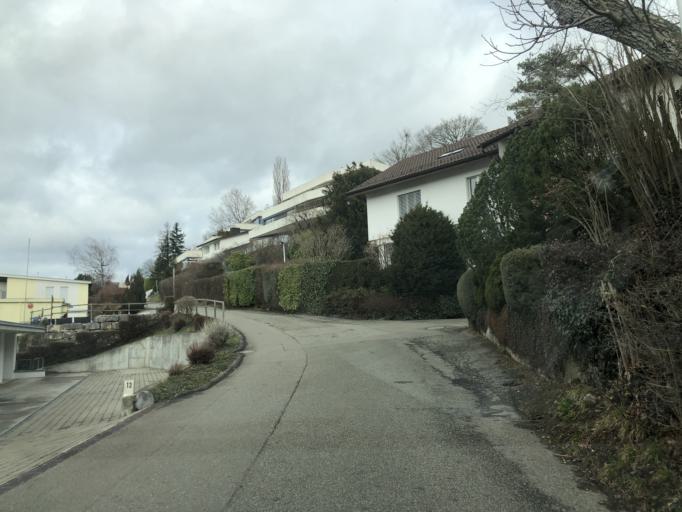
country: CH
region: Aargau
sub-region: Bezirk Baden
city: Obersiggenthal
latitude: 47.4911
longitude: 8.2946
